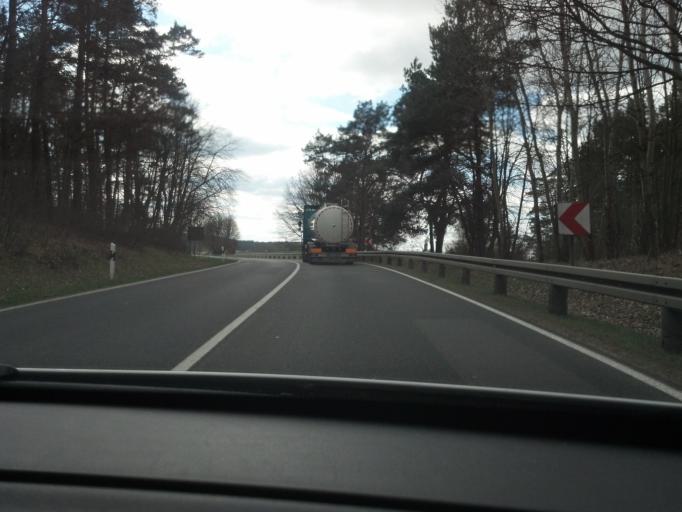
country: DE
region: Mecklenburg-Vorpommern
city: Wesenberg
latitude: 53.2914
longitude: 13.0239
